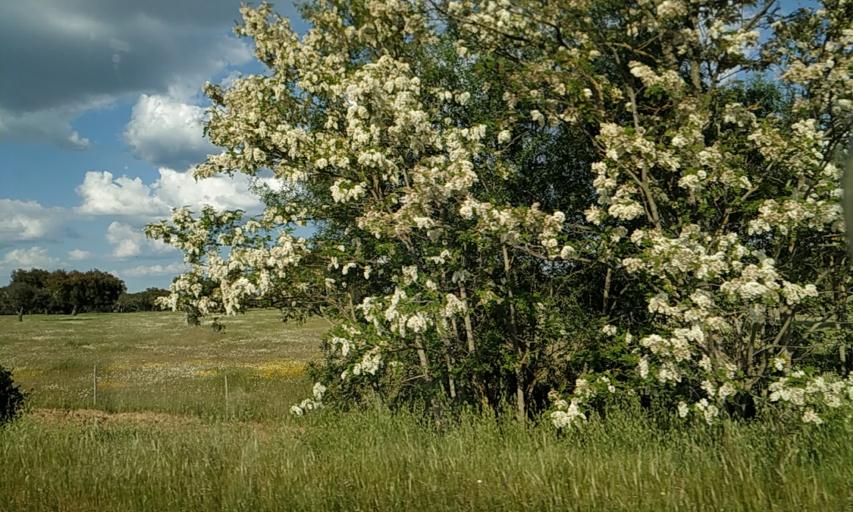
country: PT
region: Portalegre
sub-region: Portalegre
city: Urra
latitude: 39.2058
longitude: -7.4585
